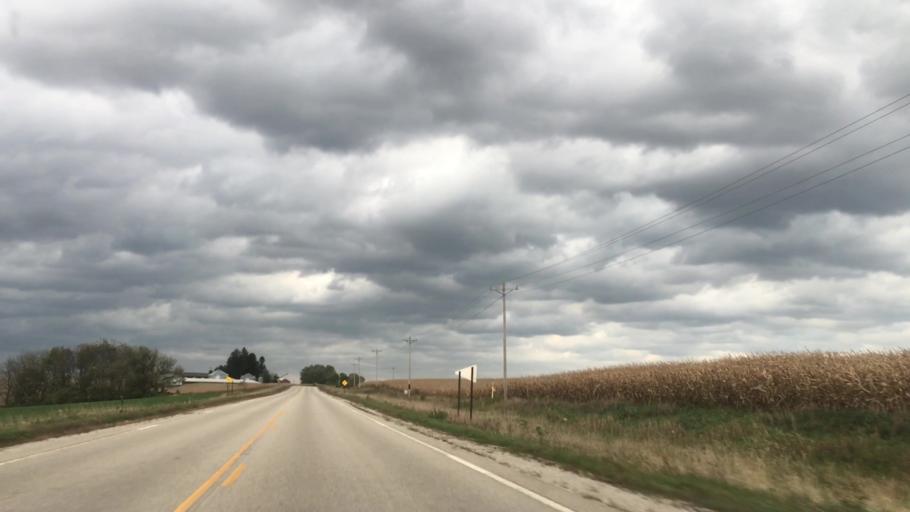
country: US
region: Minnesota
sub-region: Fillmore County
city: Preston
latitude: 43.7329
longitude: -92.0317
